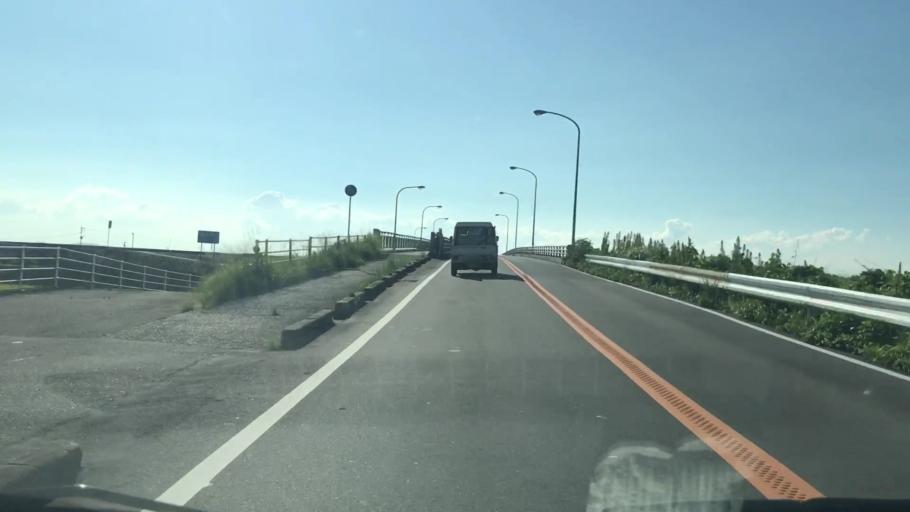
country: JP
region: Saga Prefecture
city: Saga-shi
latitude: 33.2195
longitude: 130.2541
